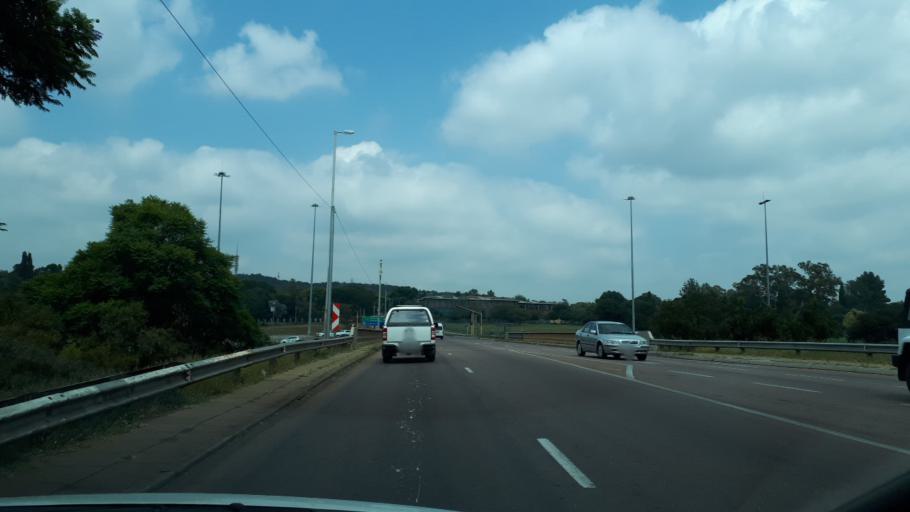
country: ZA
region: Gauteng
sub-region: City of Tshwane Metropolitan Municipality
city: Pretoria
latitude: -25.7455
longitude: 28.2927
